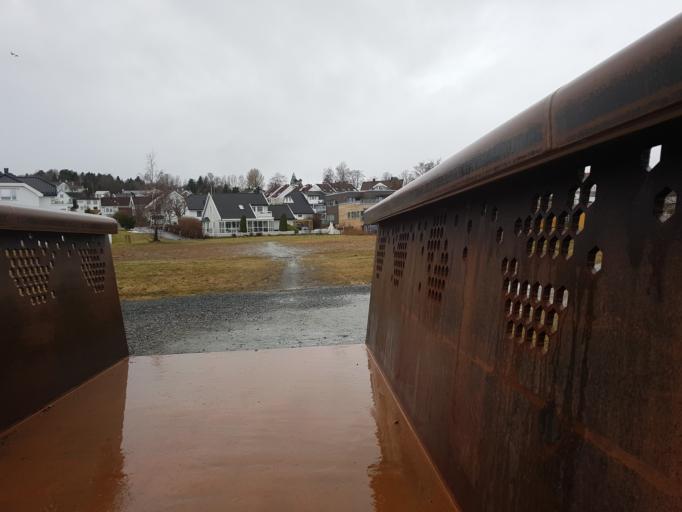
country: NO
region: Sor-Trondelag
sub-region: Trondheim
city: Trondheim
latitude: 63.4356
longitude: 10.5000
